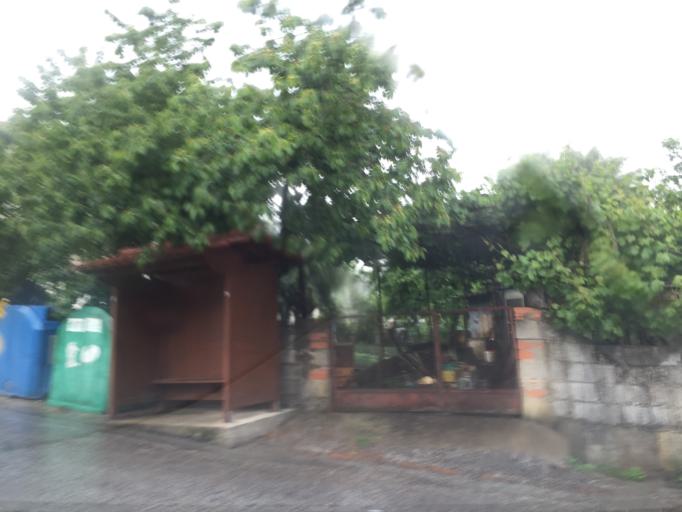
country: PT
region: Leiria
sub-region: Pedrogao Grande
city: Pedrogao Grande
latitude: 40.0174
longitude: -8.0997
